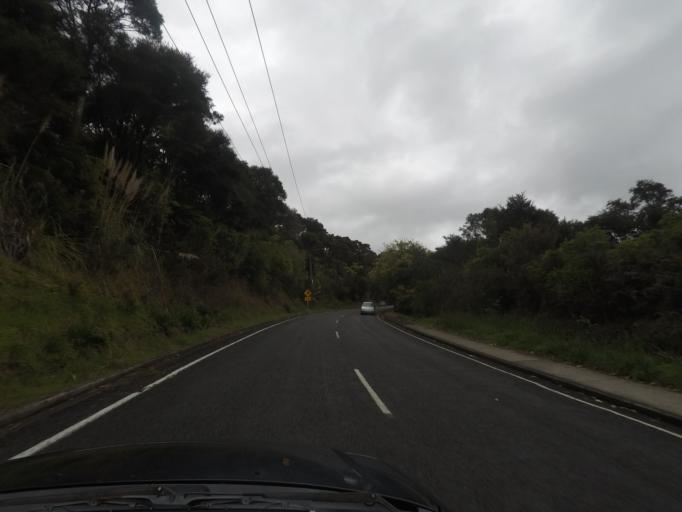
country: NZ
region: Auckland
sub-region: Auckland
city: Titirangi
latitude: -36.9270
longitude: 174.5975
